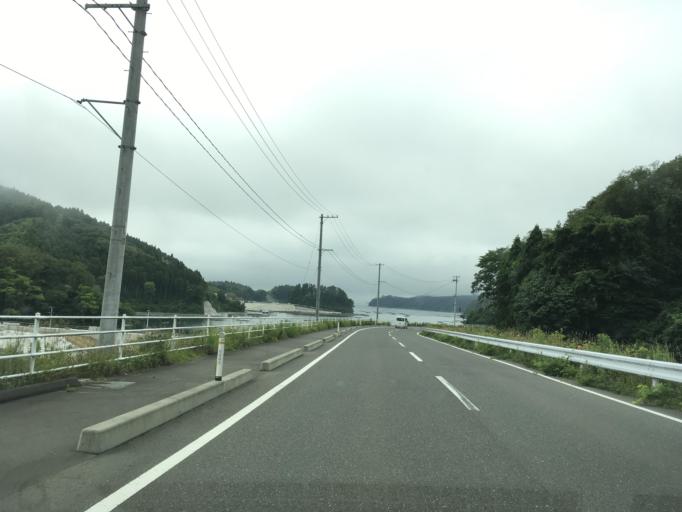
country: JP
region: Iwate
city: Ofunato
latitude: 38.9041
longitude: 141.6328
